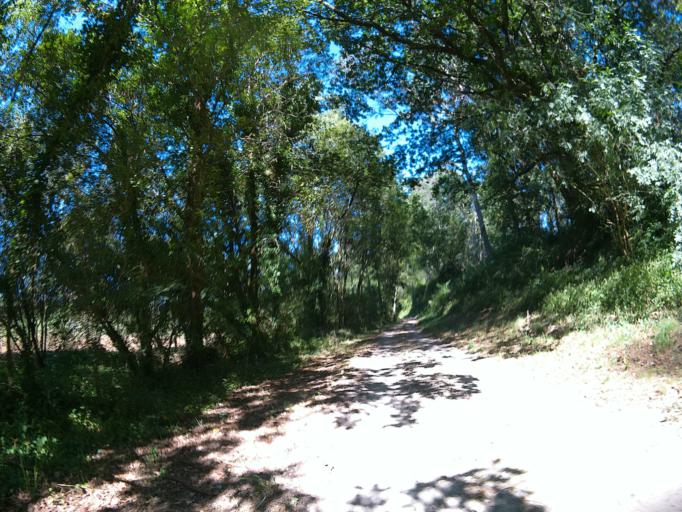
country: PT
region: Viana do Castelo
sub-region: Ponte de Lima
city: Ponte de Lima
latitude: 41.7619
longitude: -8.6094
